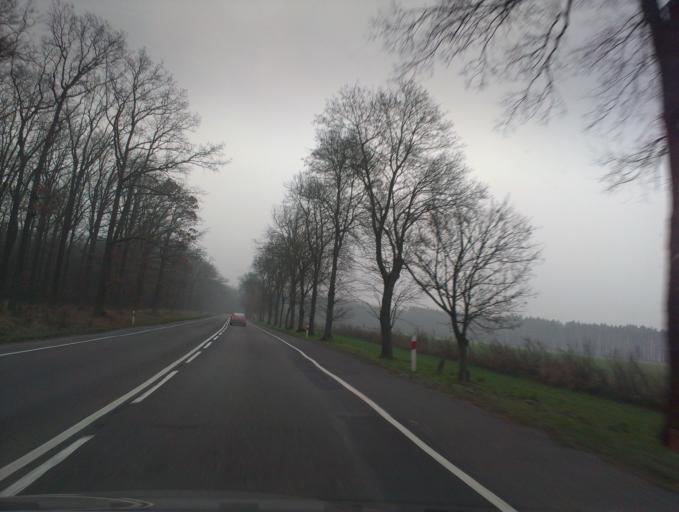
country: PL
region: Greater Poland Voivodeship
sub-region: Powiat chodzieski
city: Budzyn
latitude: 52.9247
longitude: 16.9675
